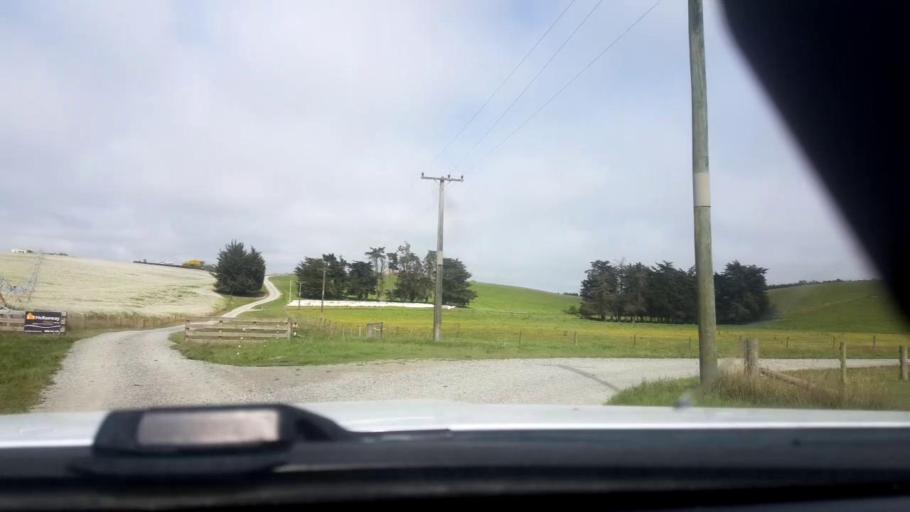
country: NZ
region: Canterbury
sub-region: Timaru District
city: Timaru
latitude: -44.3313
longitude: 171.1997
